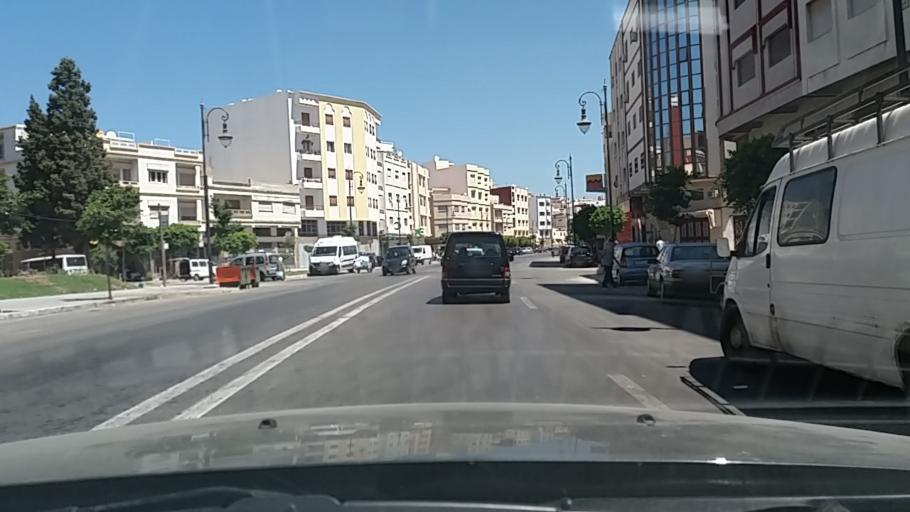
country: MA
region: Tanger-Tetouan
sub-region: Tanger-Assilah
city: Tangier
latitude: 35.7545
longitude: -5.7993
